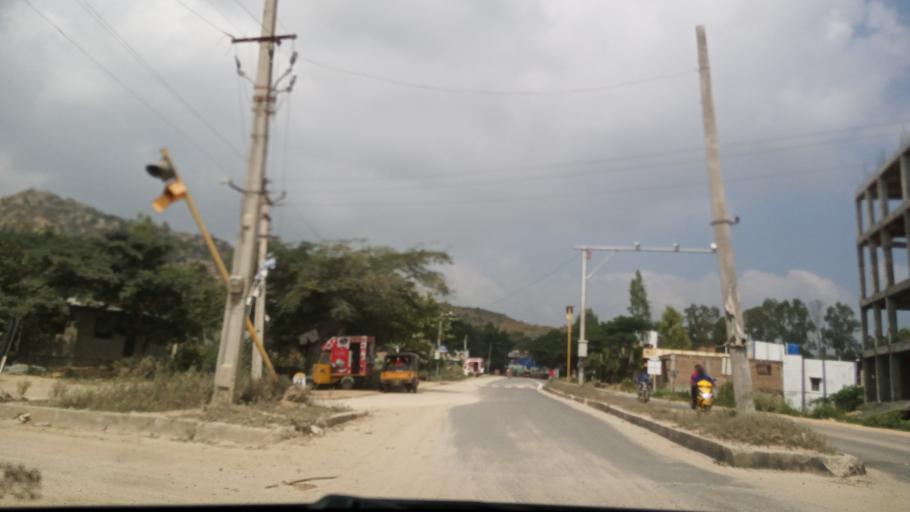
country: IN
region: Andhra Pradesh
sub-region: Chittoor
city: Madanapalle
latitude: 13.5808
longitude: 78.5210
